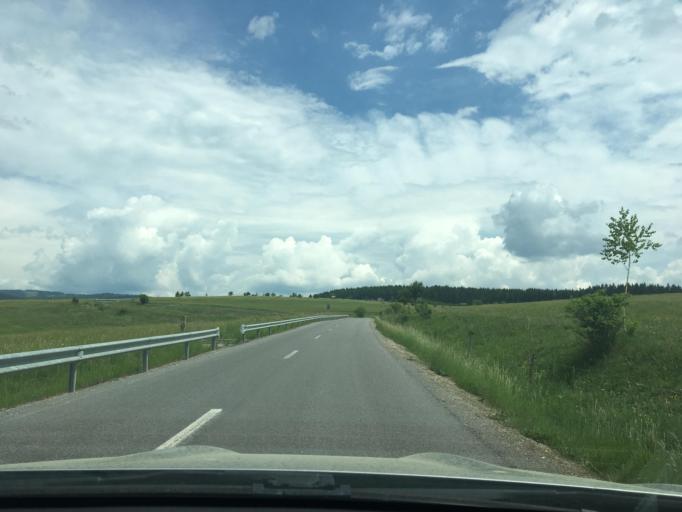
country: RO
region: Harghita
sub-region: Comuna Ditrau
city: Ditrau
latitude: 46.8463
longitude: 25.5018
